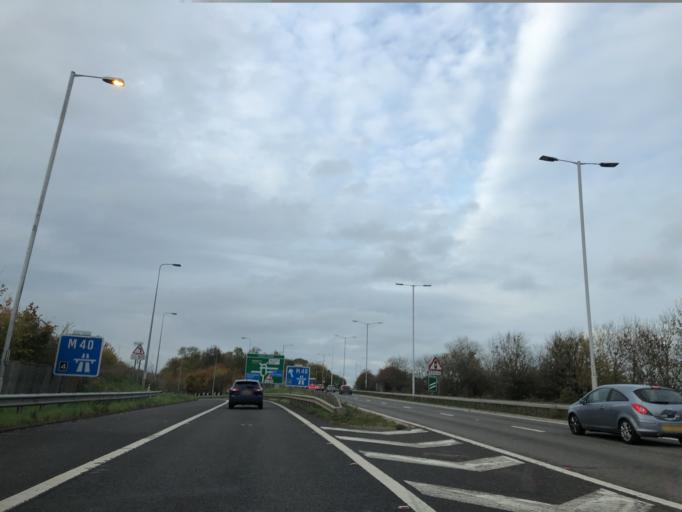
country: GB
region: England
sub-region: Buckinghamshire
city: High Wycombe
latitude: 51.6090
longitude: -0.7668
